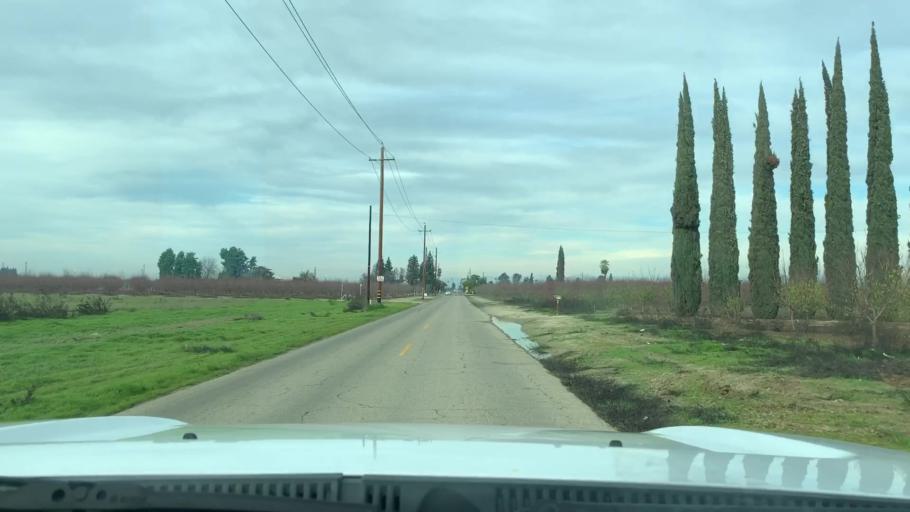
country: US
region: California
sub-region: Fresno County
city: Selma
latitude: 36.6005
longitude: -119.5748
